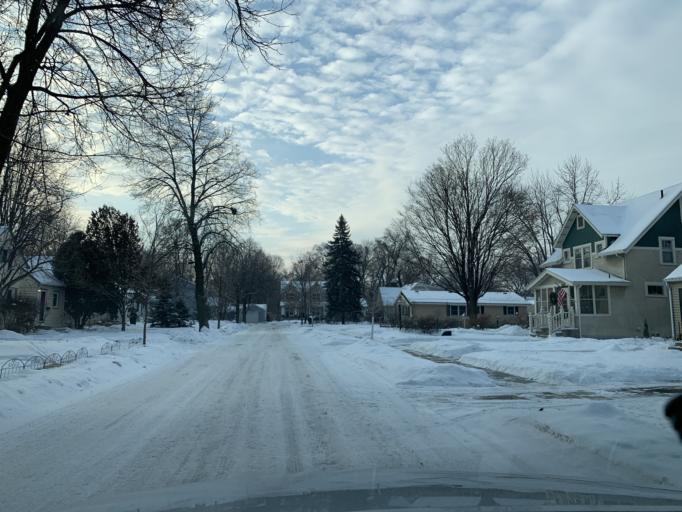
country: US
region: Minnesota
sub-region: Hennepin County
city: Saint Louis Park
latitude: 44.9251
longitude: -93.3520
